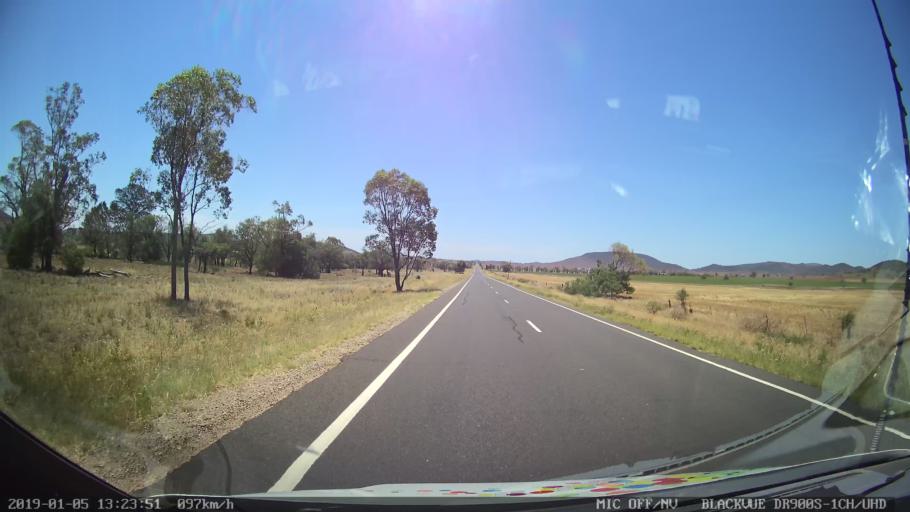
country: AU
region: New South Wales
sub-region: Gunnedah
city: Gunnedah
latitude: -31.0745
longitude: 149.9808
